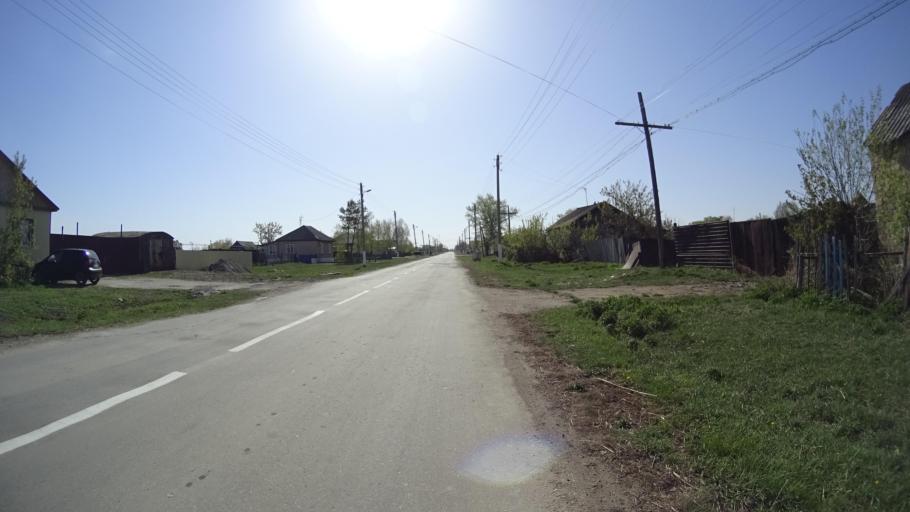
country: RU
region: Chelyabinsk
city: Chesma
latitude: 53.8003
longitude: 61.0223
